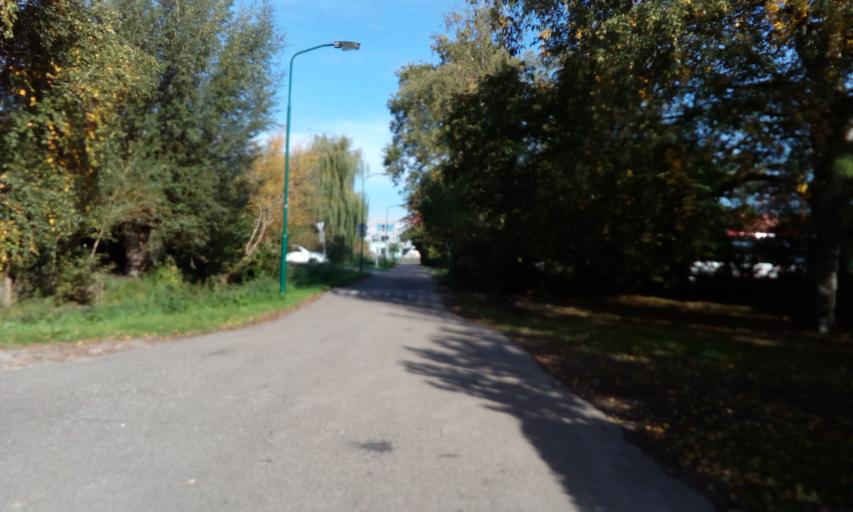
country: NL
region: Utrecht
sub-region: Stichtse Vecht
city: Maarssen
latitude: 52.0934
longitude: 5.0486
